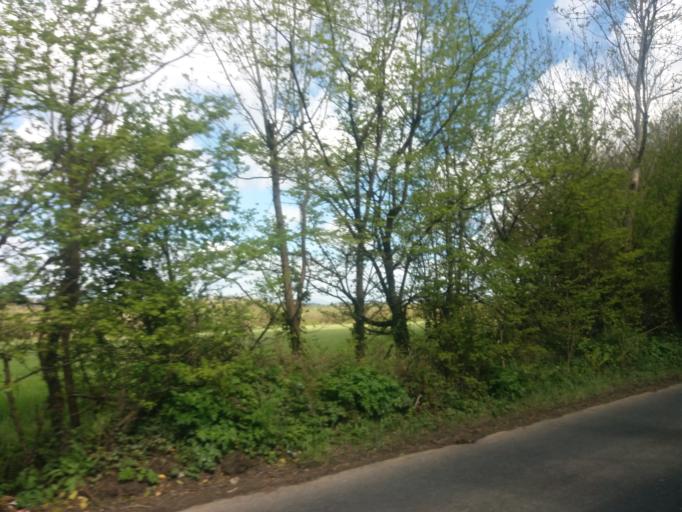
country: IE
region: Leinster
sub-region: Loch Garman
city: New Ross
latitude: 52.2780
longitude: -6.7242
